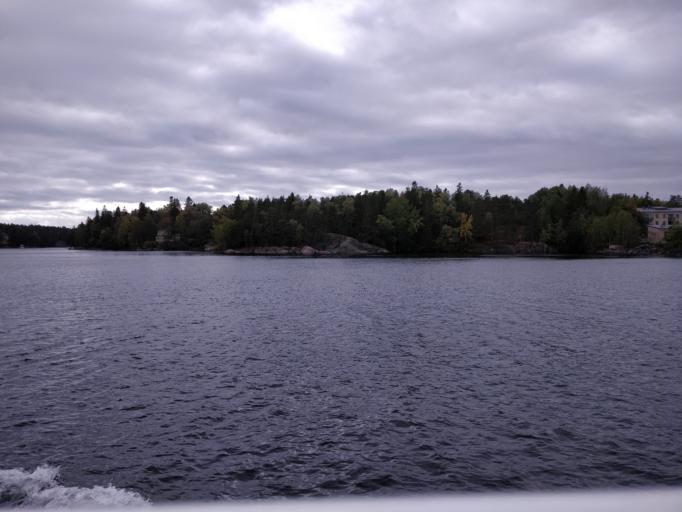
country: FI
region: Uusimaa
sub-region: Helsinki
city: Vantaa
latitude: 60.1730
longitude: 25.0877
